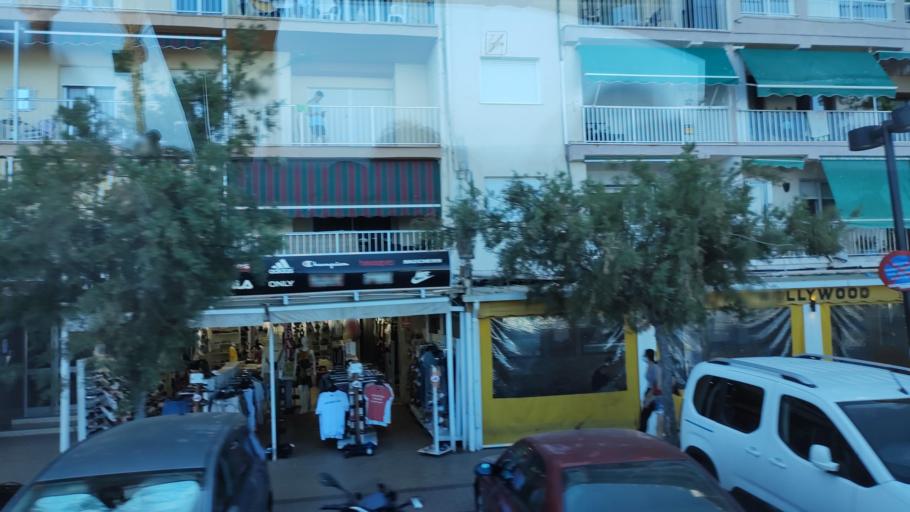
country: ES
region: Andalusia
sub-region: Provincia de Malaga
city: Fuengirola
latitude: 36.5370
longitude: -4.6222
